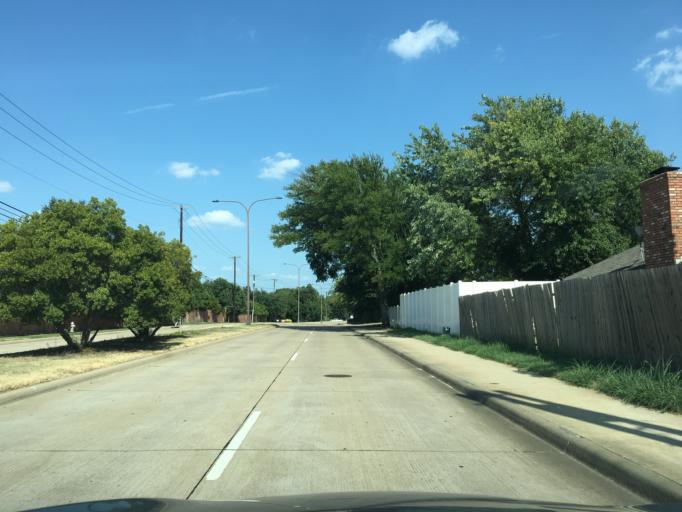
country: US
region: Texas
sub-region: Tarrant County
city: Dalworthington Gardens
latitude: 32.6801
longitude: -97.1618
